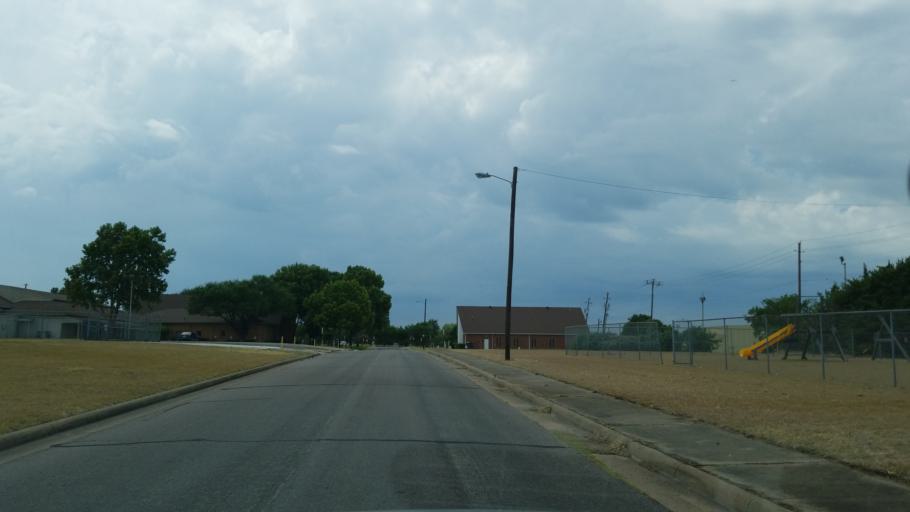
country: US
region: Texas
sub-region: Dallas County
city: Duncanville
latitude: 32.6583
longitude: -96.8546
